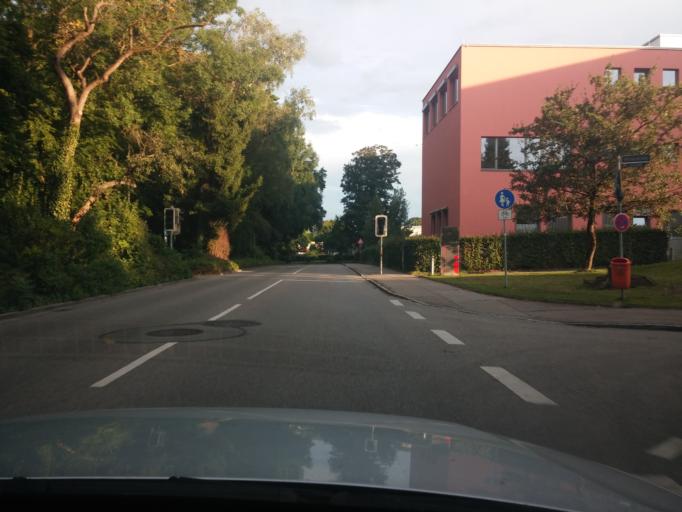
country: DE
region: Bavaria
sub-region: Swabia
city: Memmingen
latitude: 47.9811
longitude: 10.1790
